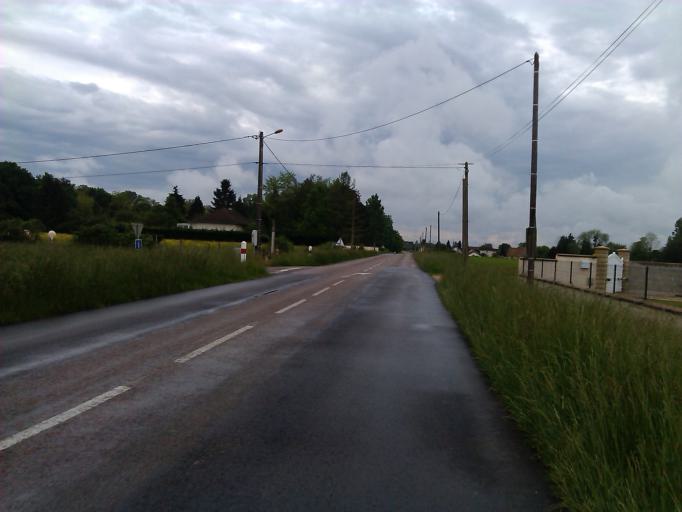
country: FR
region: Bourgogne
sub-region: Departement de Saone-et-Loire
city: Gergy
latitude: 46.8932
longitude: 4.9499
